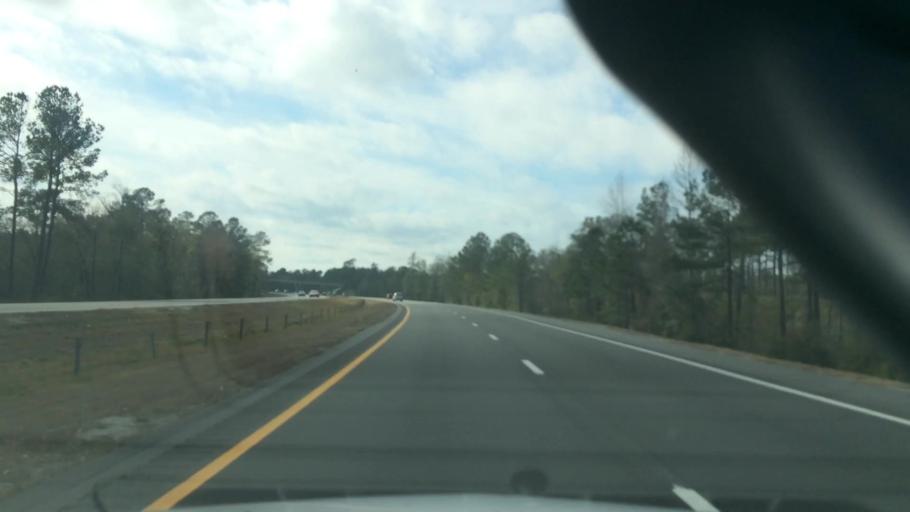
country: US
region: North Carolina
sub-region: New Hanover County
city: Wrightsboro
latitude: 34.3189
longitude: -77.9386
